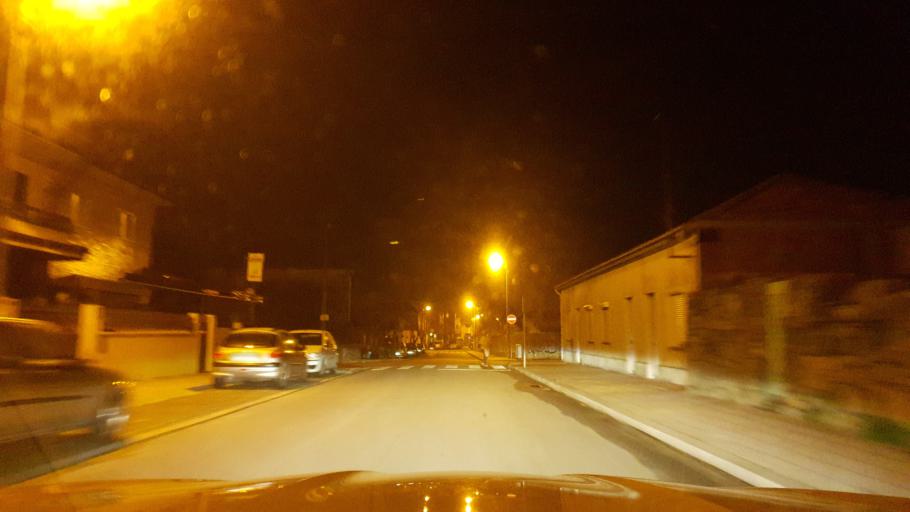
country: PT
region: Porto
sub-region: Maia
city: Leca do Bailio
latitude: 41.2127
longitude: -8.6363
